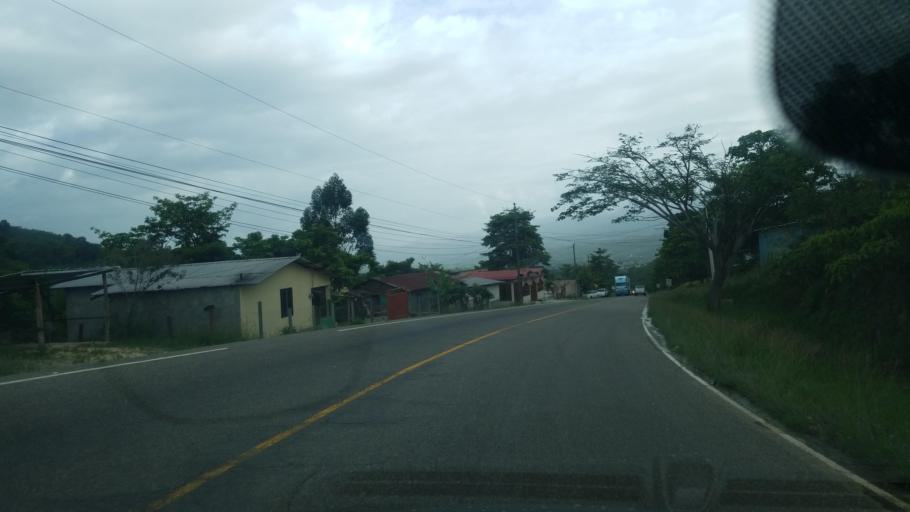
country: HN
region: Ocotepeque
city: Sinuapa
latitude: 14.4512
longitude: -89.1686
